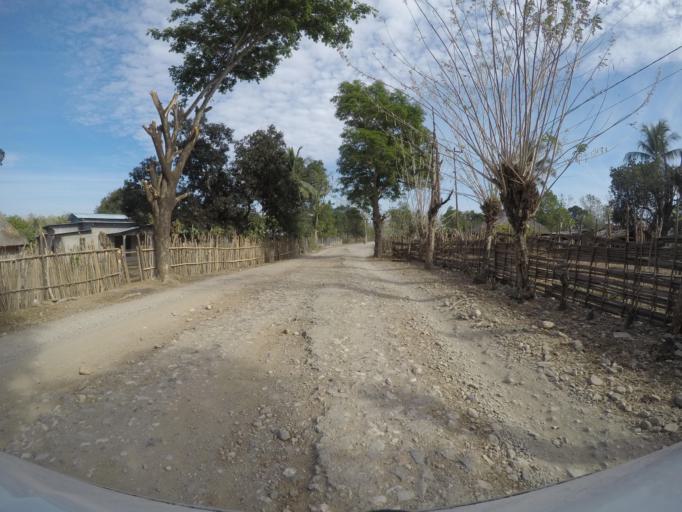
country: TL
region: Bobonaro
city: Maliana
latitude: -8.9163
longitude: 125.2156
